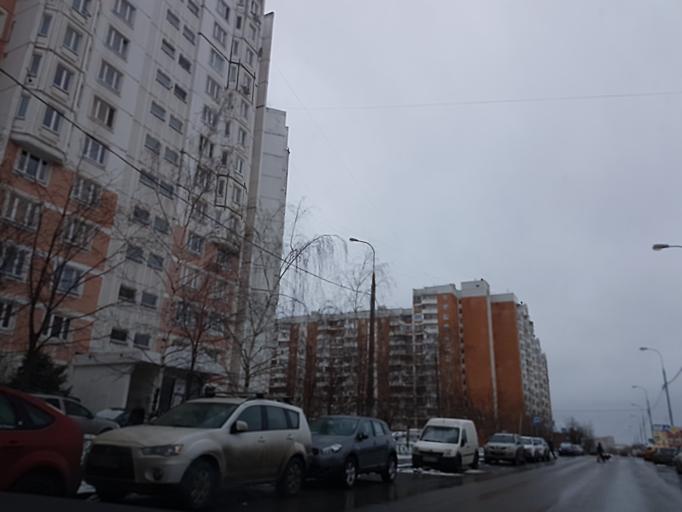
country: RU
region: Moskovskaya
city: Pavshino
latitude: 55.8317
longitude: 37.3527
